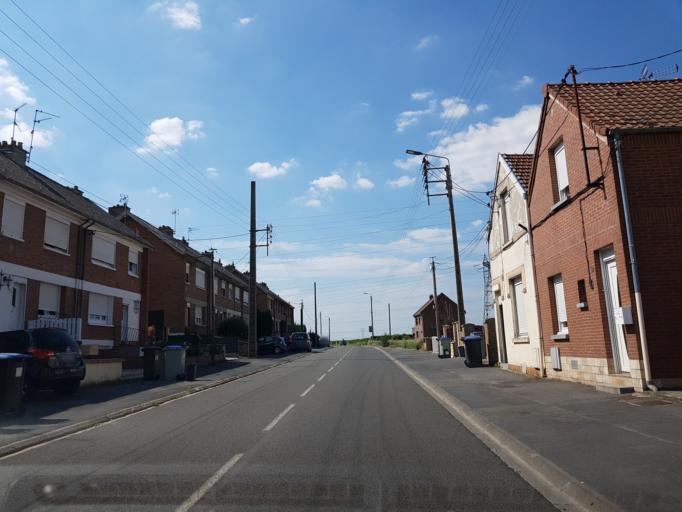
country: FR
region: Nord-Pas-de-Calais
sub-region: Departement du Nord
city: Roeulx
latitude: 50.3134
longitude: 3.3324
